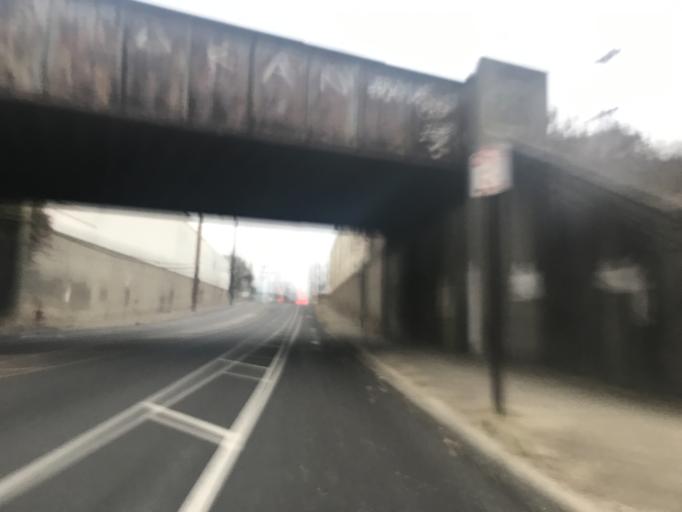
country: US
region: Kentucky
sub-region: Jefferson County
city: Louisville
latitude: 38.2272
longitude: -85.7731
